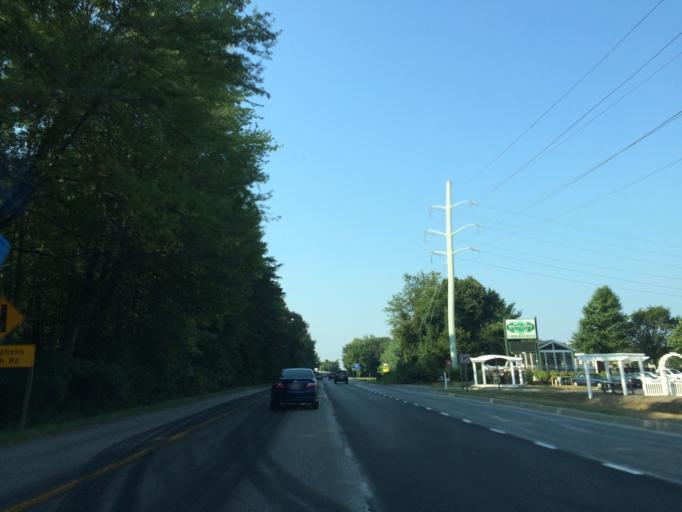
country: US
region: Maryland
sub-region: Anne Arundel County
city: Gambrills
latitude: 39.0465
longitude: -76.6664
